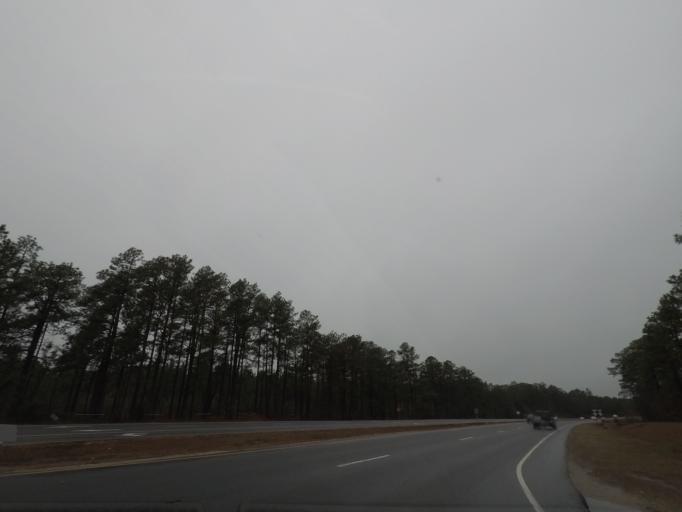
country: US
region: North Carolina
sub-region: Cumberland County
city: Spring Lake
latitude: 35.2314
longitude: -79.0164
